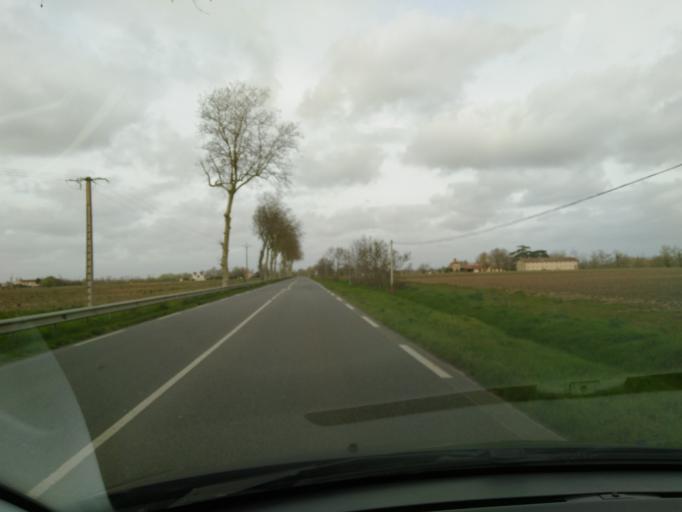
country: FR
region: Midi-Pyrenees
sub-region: Departement de la Haute-Garonne
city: Merville
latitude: 43.7403
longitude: 1.3117
